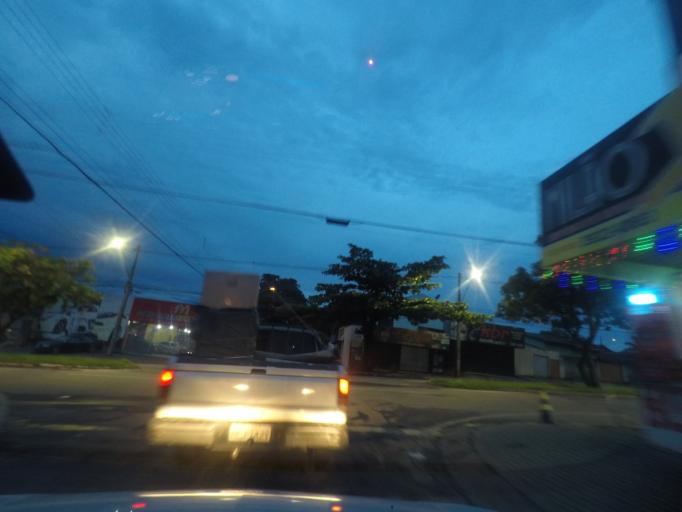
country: BR
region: Goias
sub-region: Goiania
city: Goiania
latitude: -16.7096
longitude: -49.3162
